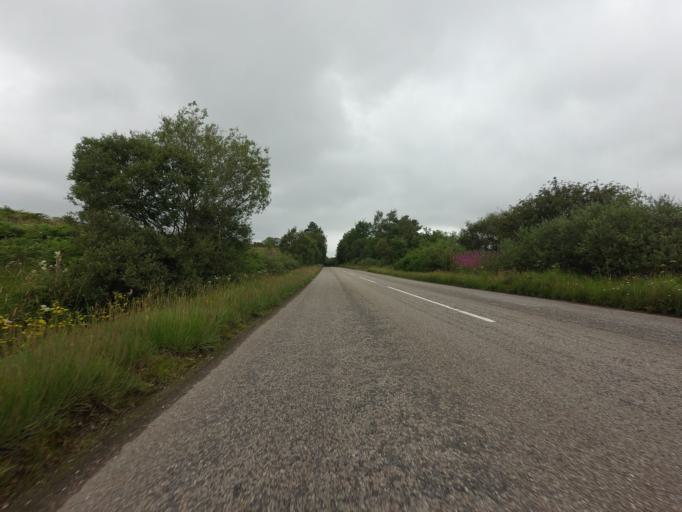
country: GB
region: Scotland
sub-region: Highland
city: Alness
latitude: 58.0148
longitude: -4.4048
